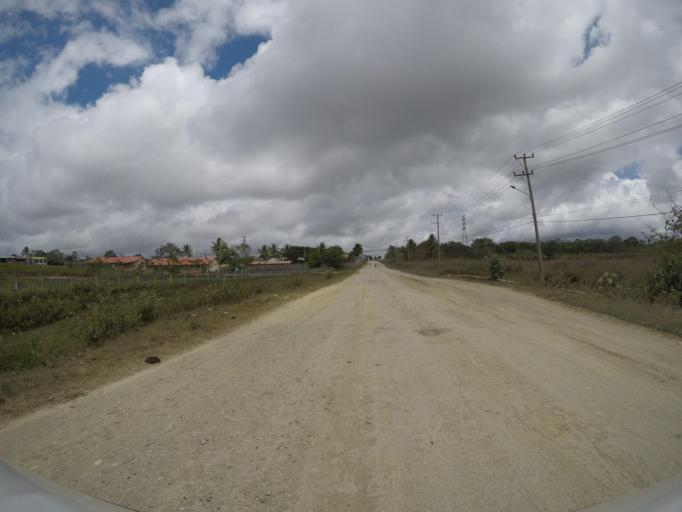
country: TL
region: Lautem
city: Lospalos
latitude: -8.4889
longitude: 126.9927
